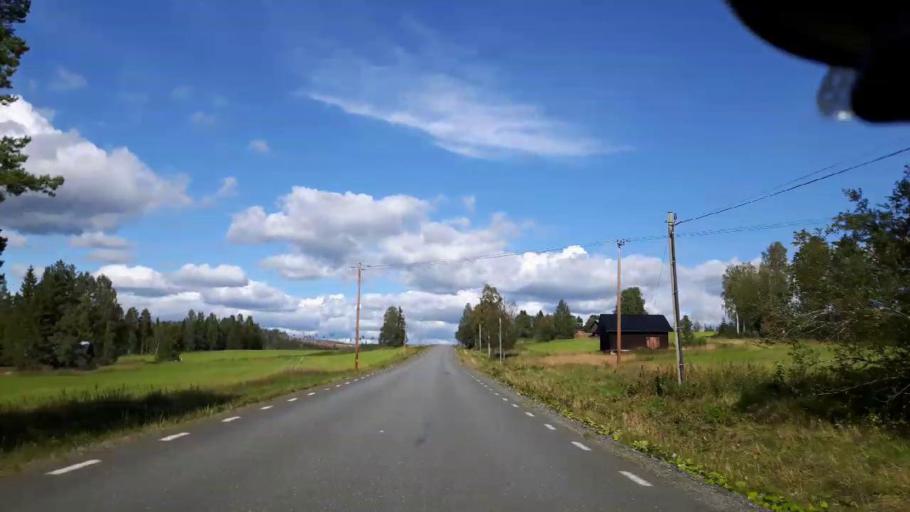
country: SE
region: Jaemtland
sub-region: Braecke Kommun
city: Braecke
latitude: 63.1855
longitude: 15.5587
